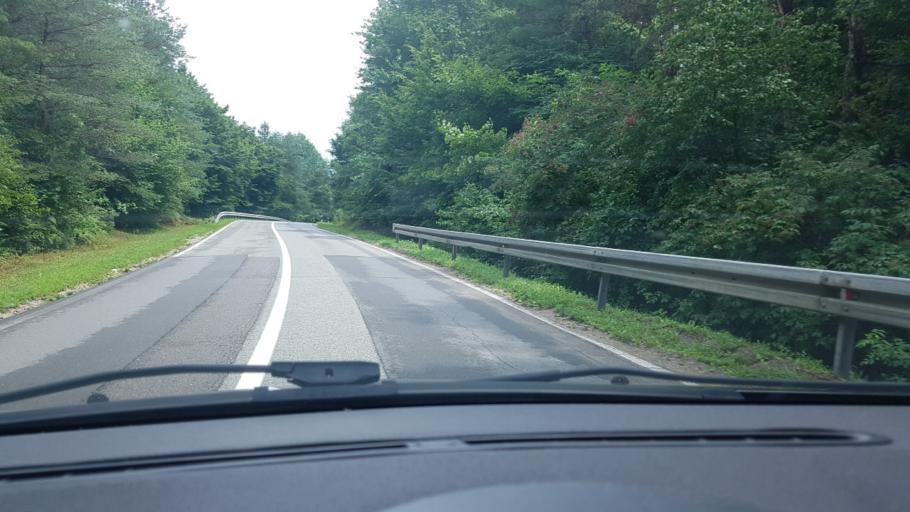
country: HR
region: Licko-Senjska
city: Jezerce
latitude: 44.9375
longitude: 15.6856
